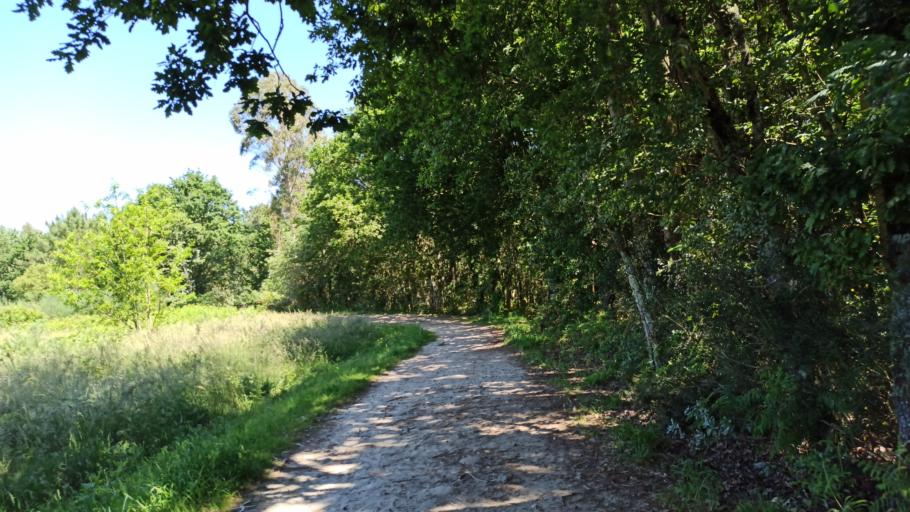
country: ES
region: Galicia
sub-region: Provincia da Coruna
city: Negreira
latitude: 42.9148
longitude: -8.7305
